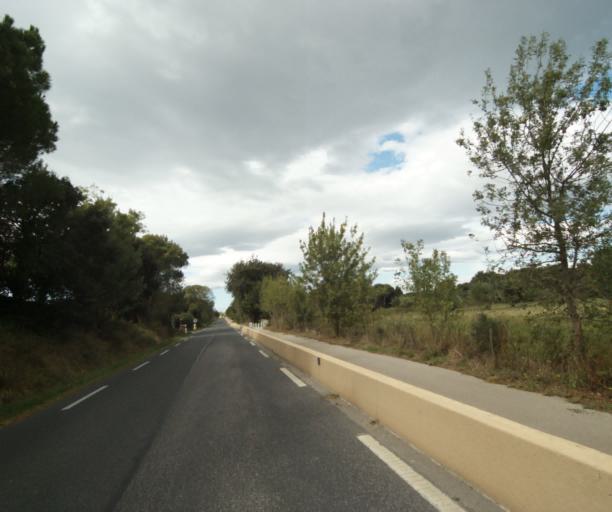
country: FR
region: Languedoc-Roussillon
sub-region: Departement des Pyrenees-Orientales
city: Argelers
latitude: 42.5368
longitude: 3.0448
